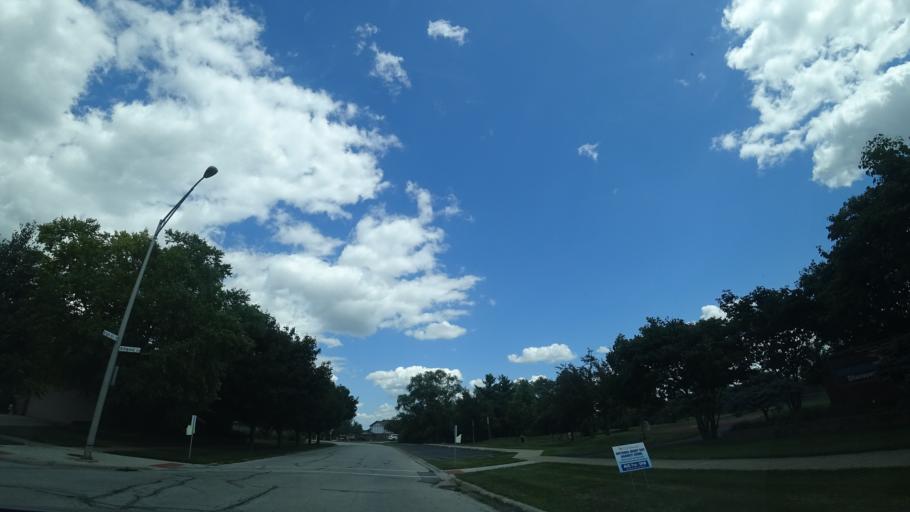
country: US
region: Illinois
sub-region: Will County
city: Homer Glen
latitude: 41.5764
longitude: -87.8982
